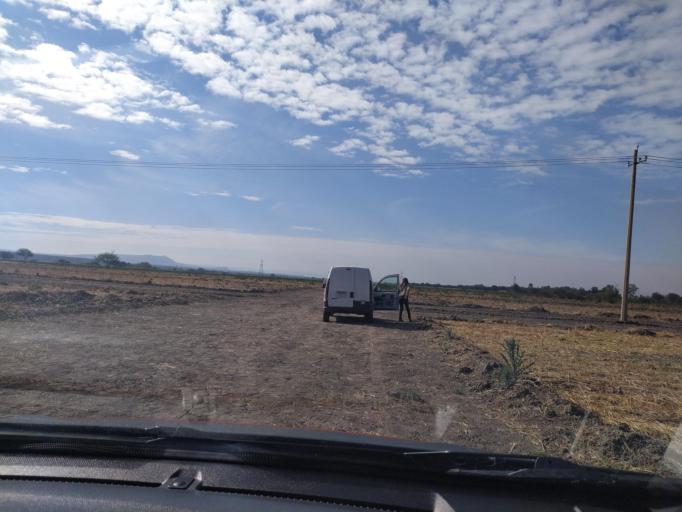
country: MX
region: Guanajuato
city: San Roque
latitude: 20.9454
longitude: -101.8619
